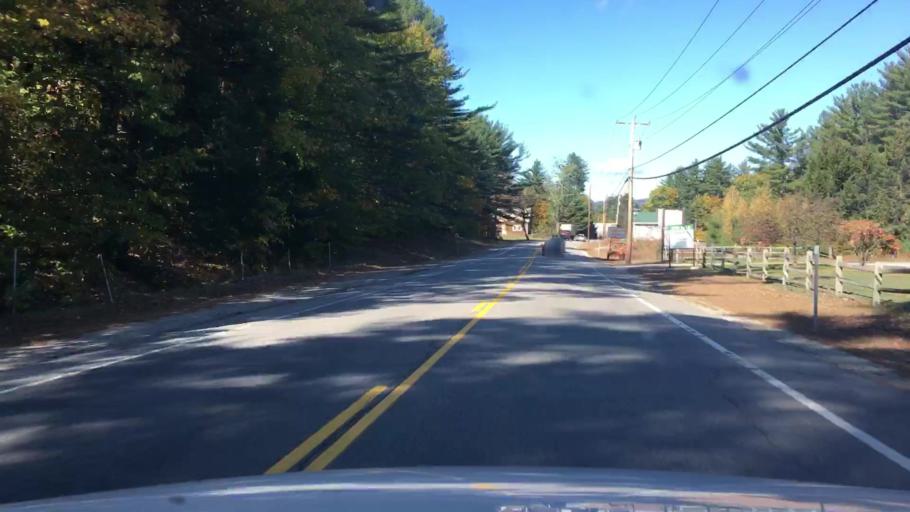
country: US
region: New Hampshire
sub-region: Carroll County
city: Tamworth
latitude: 43.8641
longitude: -71.2114
